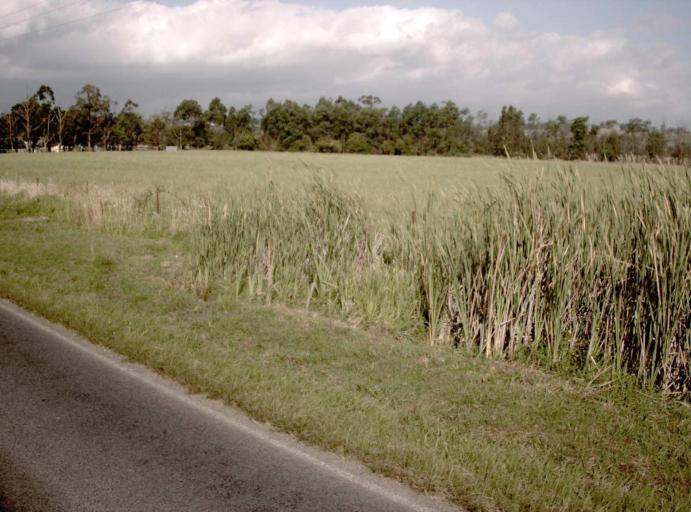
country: AU
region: Victoria
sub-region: Cardinia
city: Bunyip
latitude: -38.1209
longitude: 145.7632
